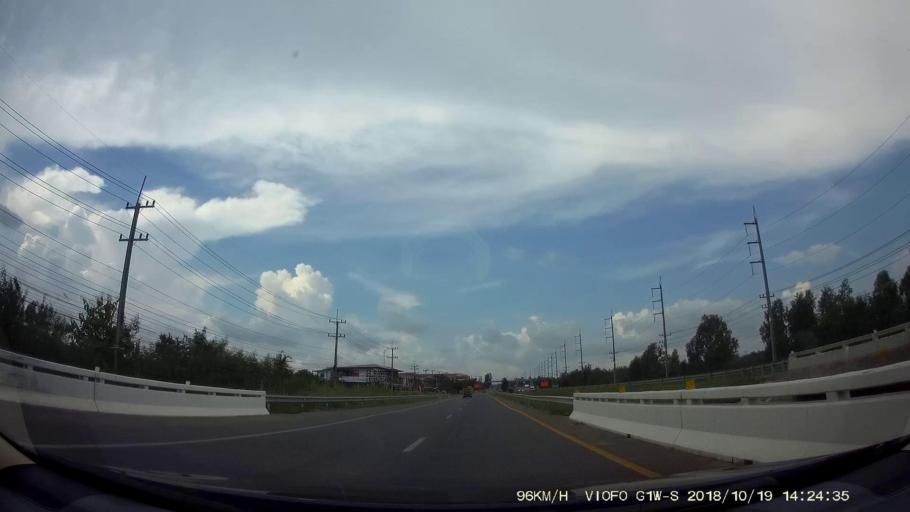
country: TH
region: Chaiyaphum
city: Kaeng Khro
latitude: 16.0830
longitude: 102.2717
